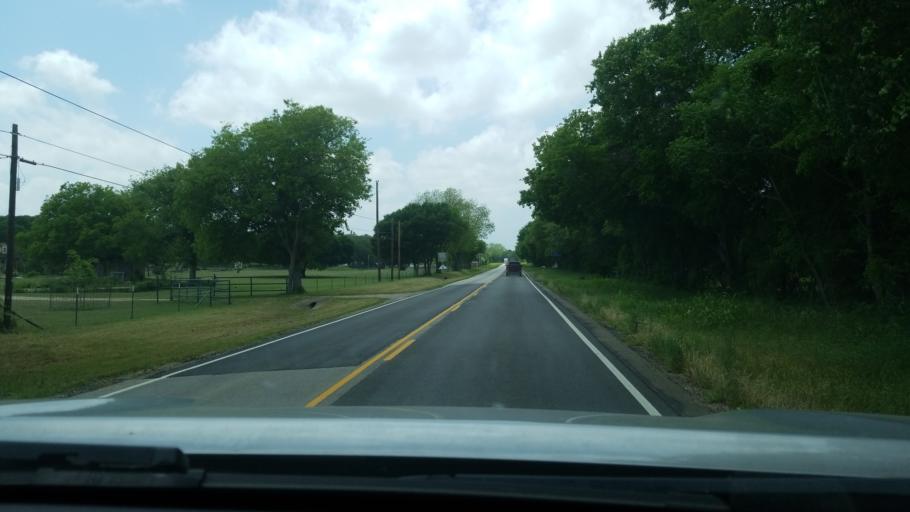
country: US
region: Texas
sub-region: Hays County
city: Dripping Springs
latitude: 30.1462
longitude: -98.0379
